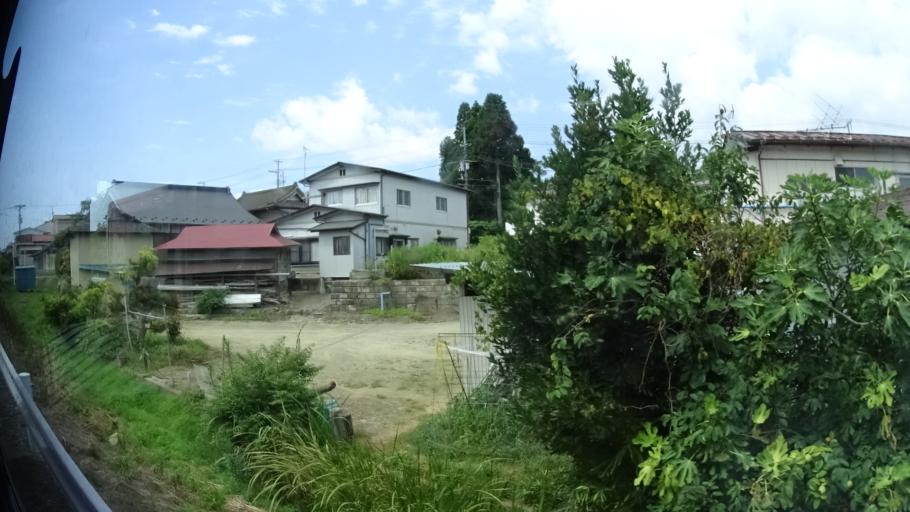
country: JP
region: Iwate
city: Ofunato
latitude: 38.8448
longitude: 141.5818
